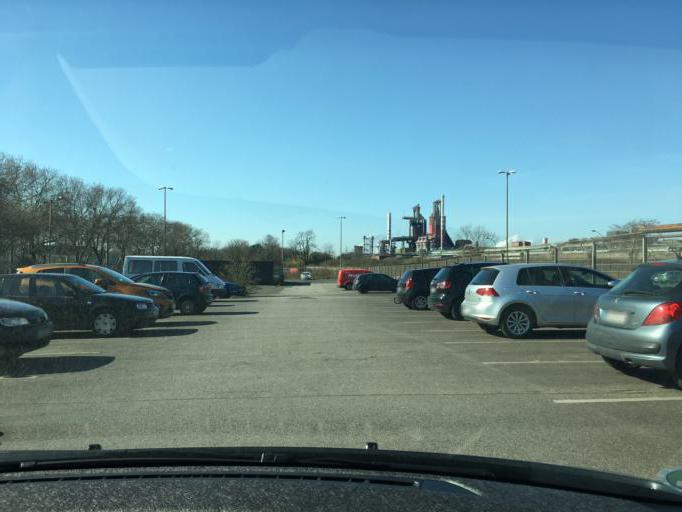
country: DE
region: North Rhine-Westphalia
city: Meiderich
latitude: 51.4902
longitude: 6.7392
